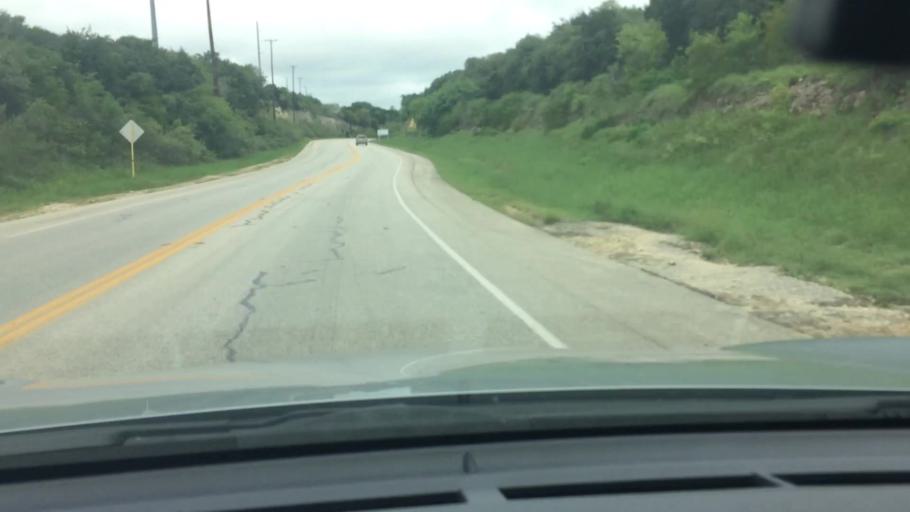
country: US
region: Texas
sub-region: Bexar County
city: Live Oak
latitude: 29.6043
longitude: -98.3668
